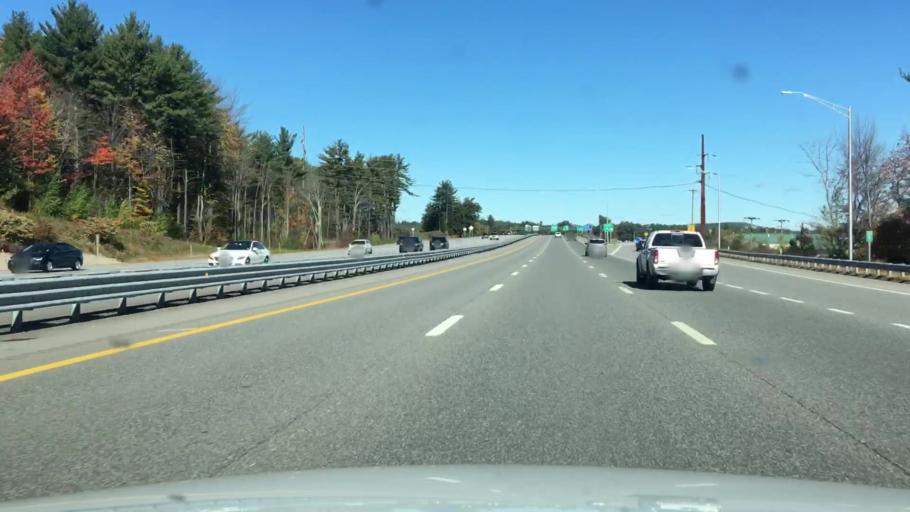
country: US
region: New Hampshire
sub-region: Strafford County
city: Rochester
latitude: 43.3082
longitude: -70.9954
